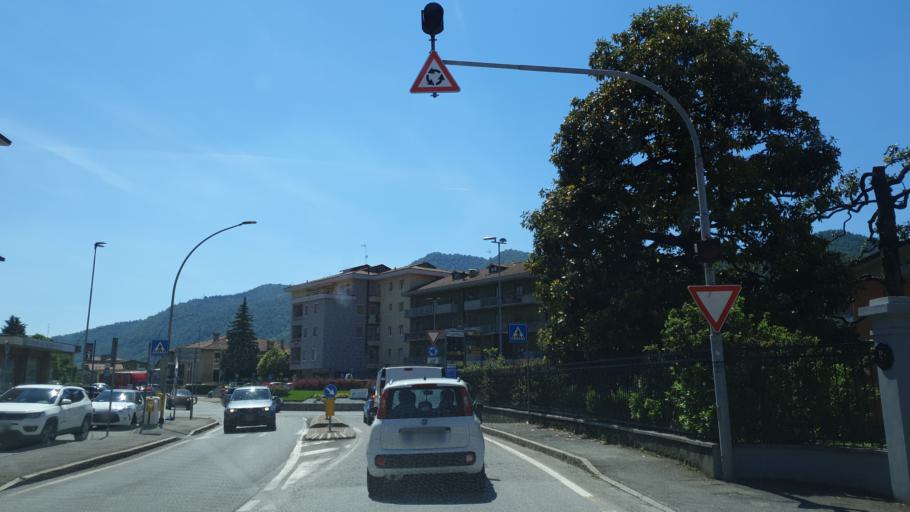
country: IT
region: Lombardy
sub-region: Provincia di Bergamo
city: Cisano Bergamasco
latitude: 45.7413
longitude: 9.4706
